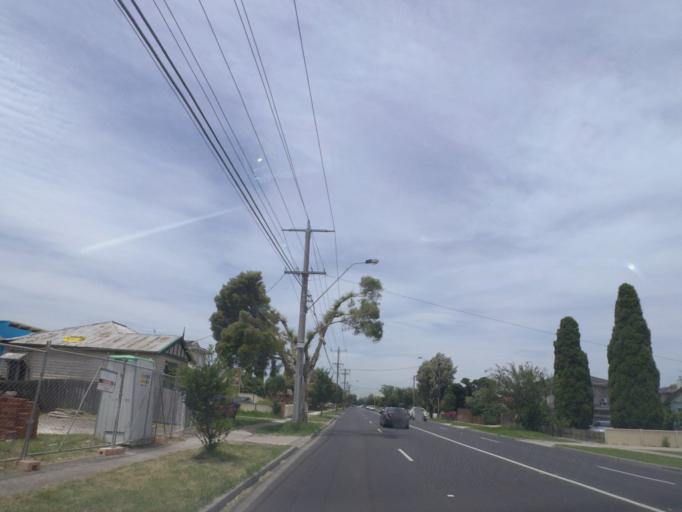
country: AU
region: Victoria
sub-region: Maribyrnong
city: Maidstone
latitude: -37.7834
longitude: 144.8706
